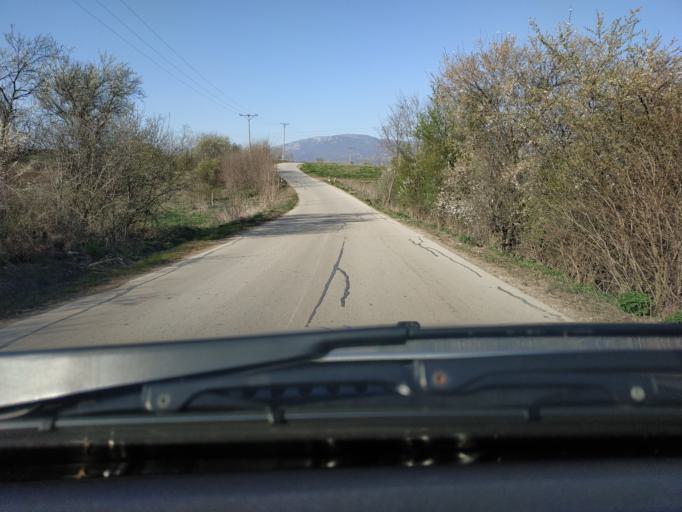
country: RS
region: Central Serbia
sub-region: Nisavski Okrug
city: Aleksinac
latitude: 43.4987
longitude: 21.7882
